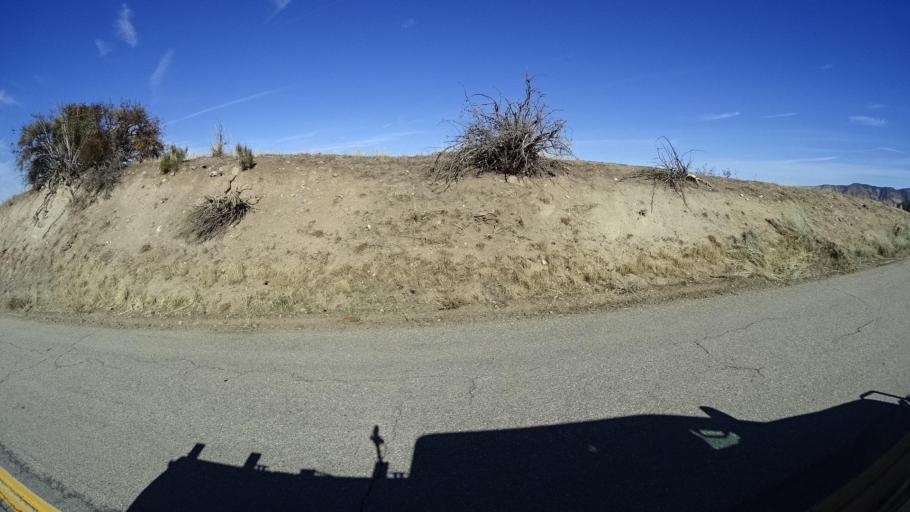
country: US
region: California
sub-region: Kern County
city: Pine Mountain Club
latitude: 34.8723
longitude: -119.3363
